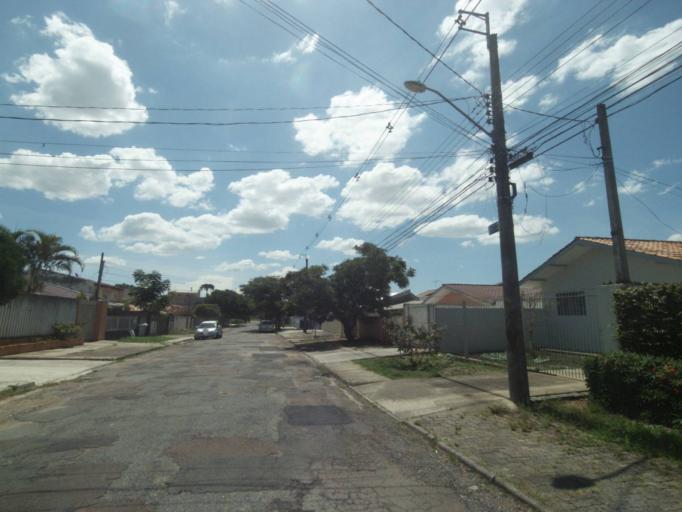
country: BR
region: Parana
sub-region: Curitiba
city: Curitiba
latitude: -25.4733
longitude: -49.2428
